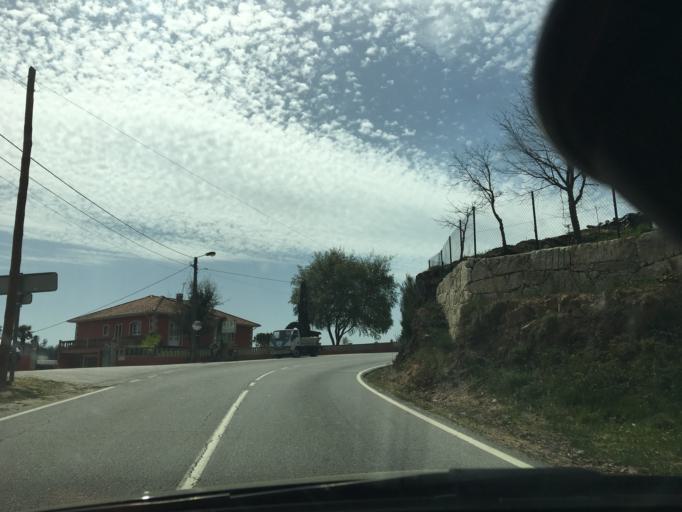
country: PT
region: Vila Real
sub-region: Boticas
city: Boticas
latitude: 41.6820
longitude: -7.6953
